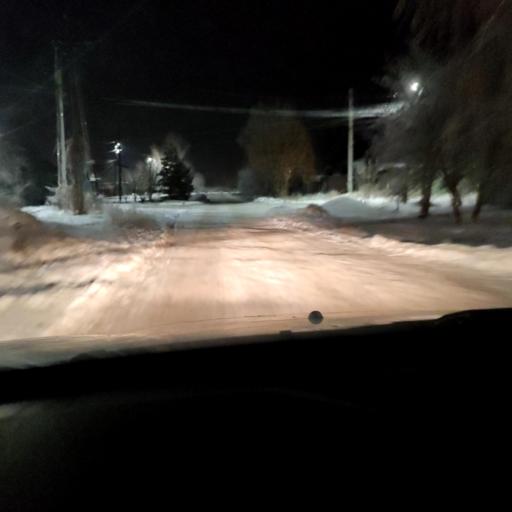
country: RU
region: Samara
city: Smyshlyayevka
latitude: 53.2394
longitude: 50.3184
